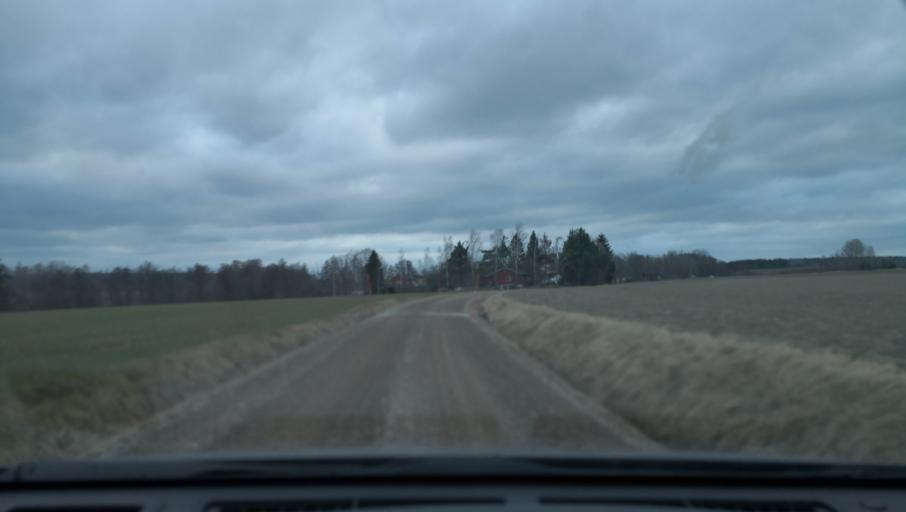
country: SE
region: Vaestmanland
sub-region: Kopings Kommun
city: Kolsva
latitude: 59.5382
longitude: 15.8934
